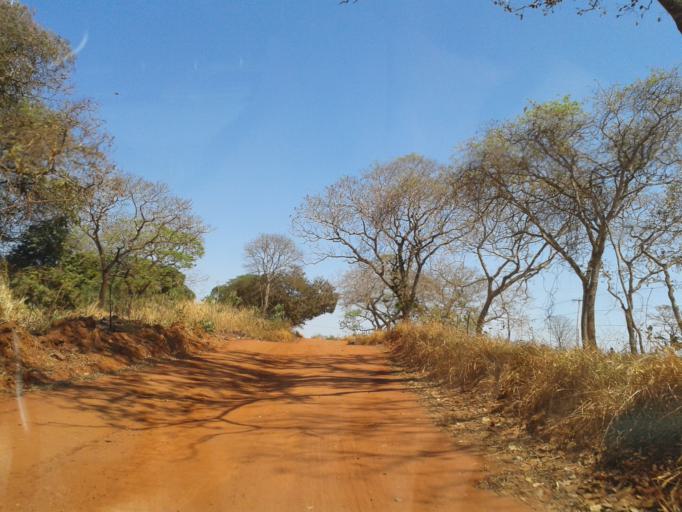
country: BR
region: Minas Gerais
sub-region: Ituiutaba
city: Ituiutaba
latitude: -18.9775
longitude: -49.4318
